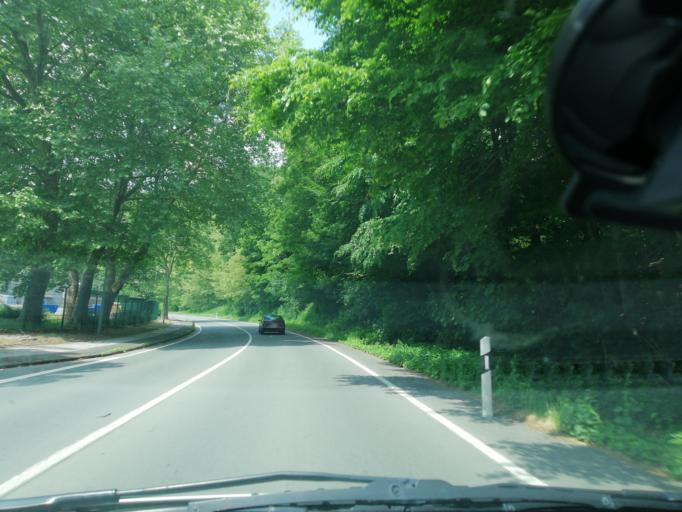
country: DE
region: North Rhine-Westphalia
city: Herdecke
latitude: 51.4034
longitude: 7.4186
